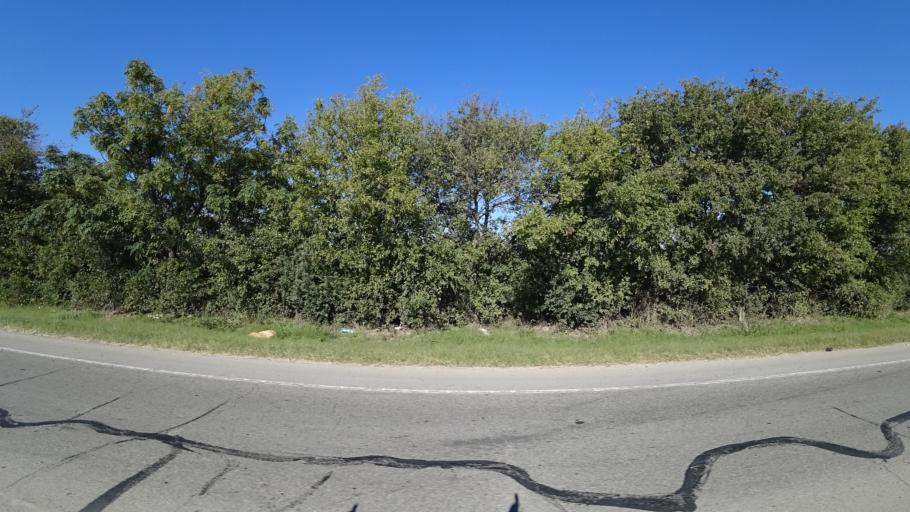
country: US
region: Texas
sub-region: Travis County
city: Hornsby Bend
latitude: 30.2382
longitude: -97.6238
